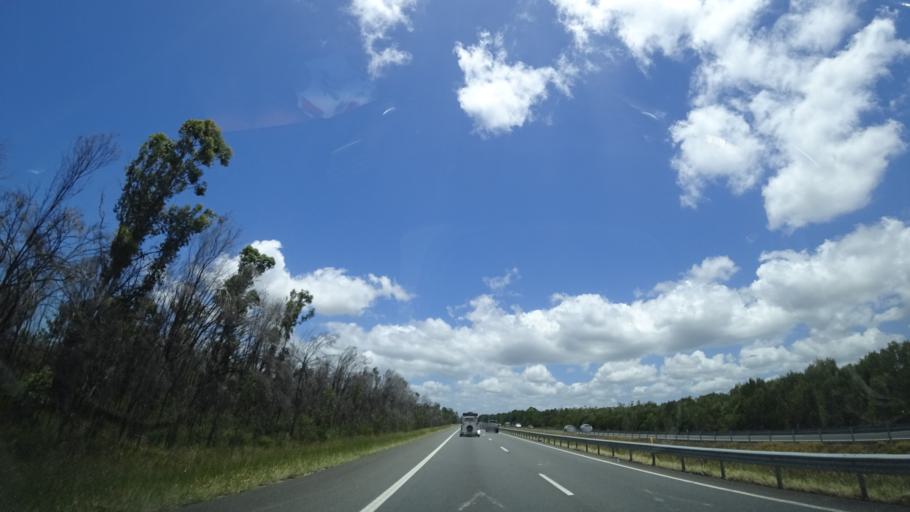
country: AU
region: Queensland
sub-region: Sunshine Coast
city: Little Mountain
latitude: -26.8031
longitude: 153.0416
